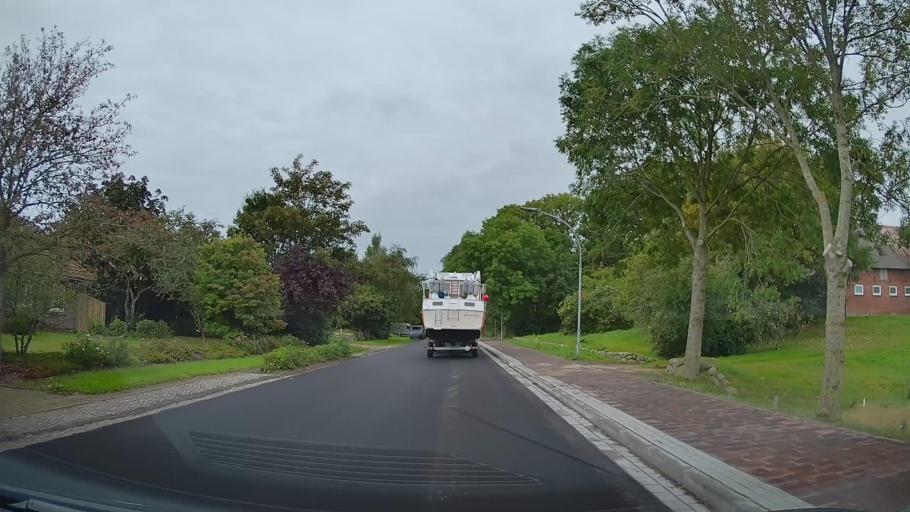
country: DE
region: Schleswig-Holstein
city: Emmelsbull-Horsbull
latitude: 54.8102
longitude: 8.6996
